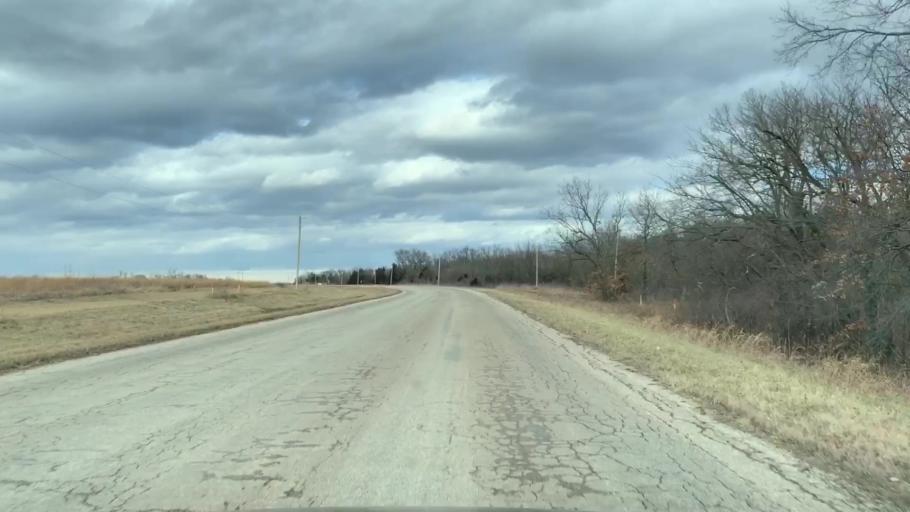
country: US
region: Kansas
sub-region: Allen County
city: Humboldt
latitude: 37.7599
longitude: -95.4712
